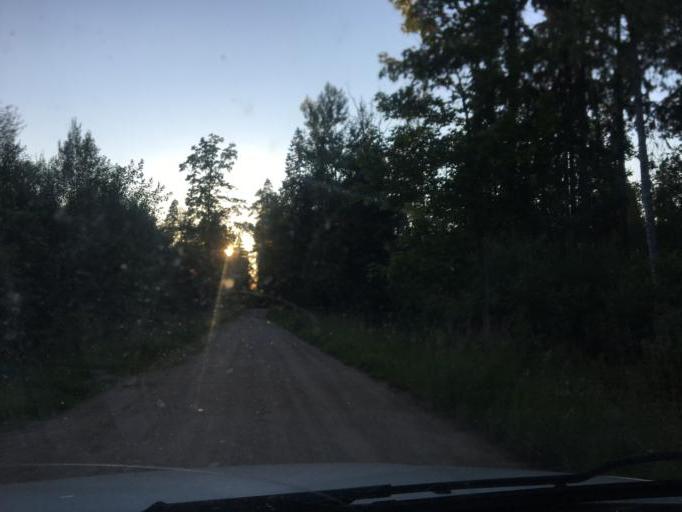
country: LV
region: Kuldigas Rajons
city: Kuldiga
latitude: 56.9805
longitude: 22.0273
